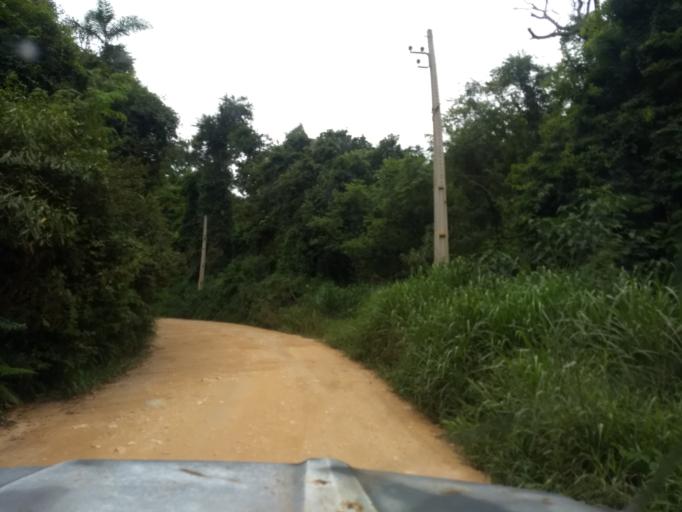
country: BR
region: Sao Paulo
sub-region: Cabreuva
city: Cabreuva
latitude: -23.4172
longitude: -47.1953
